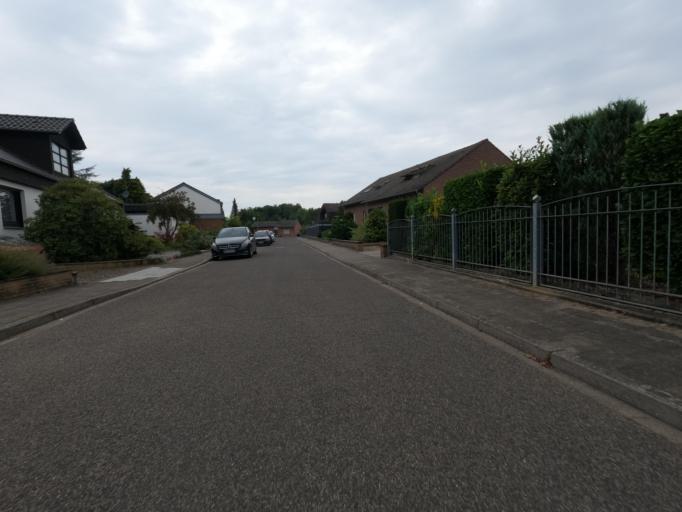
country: DE
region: North Rhine-Westphalia
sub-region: Regierungsbezirk Koln
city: Aldenhoven
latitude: 50.9438
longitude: 6.3112
